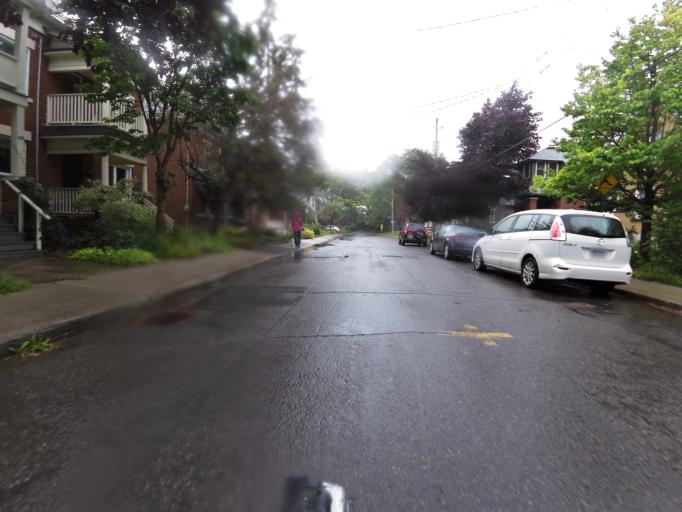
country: CA
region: Ontario
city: Ottawa
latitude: 45.4117
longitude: -75.6768
